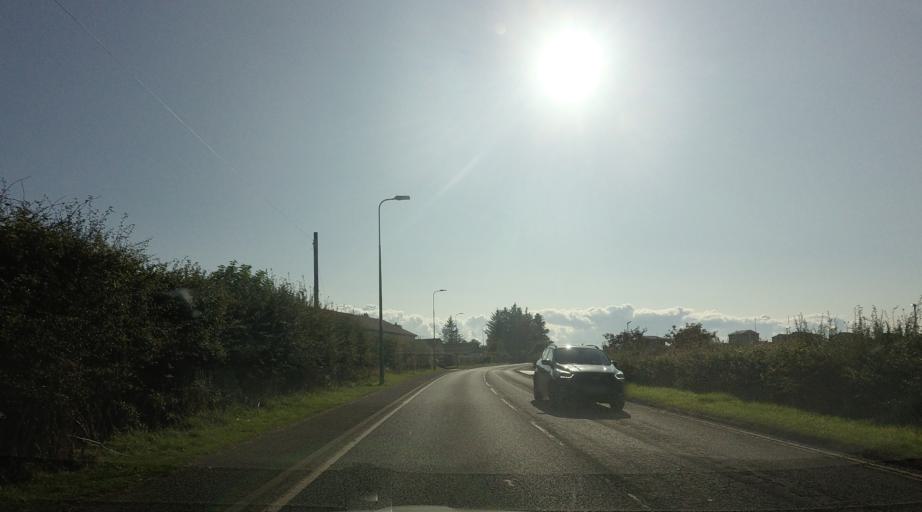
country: GB
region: Scotland
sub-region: Highland
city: Thurso
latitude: 58.5904
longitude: -3.5165
